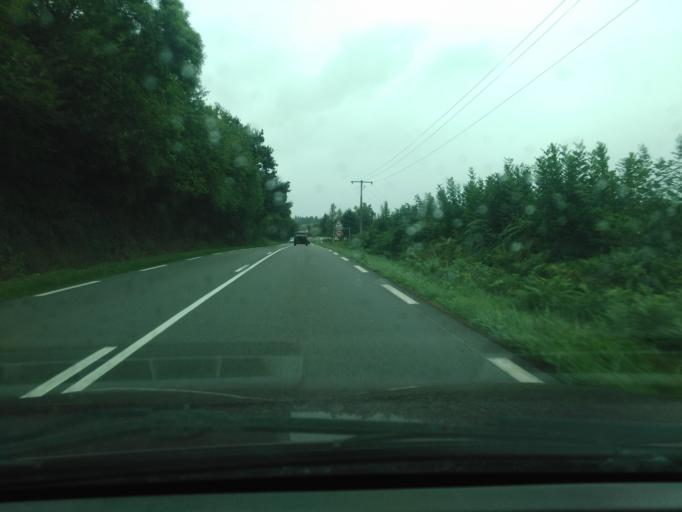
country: FR
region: Pays de la Loire
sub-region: Departement de la Vendee
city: Sainte-Hermine
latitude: 46.5842
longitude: -1.1147
